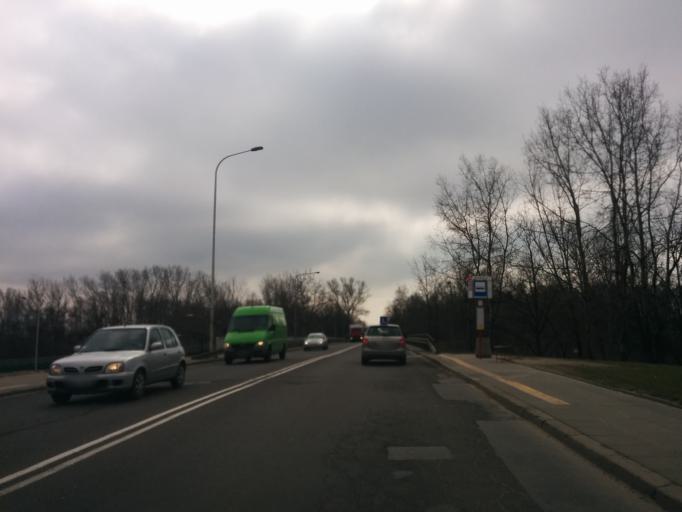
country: PL
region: Masovian Voivodeship
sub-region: Warszawa
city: Bialoleka
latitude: 52.3139
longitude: 21.0013
